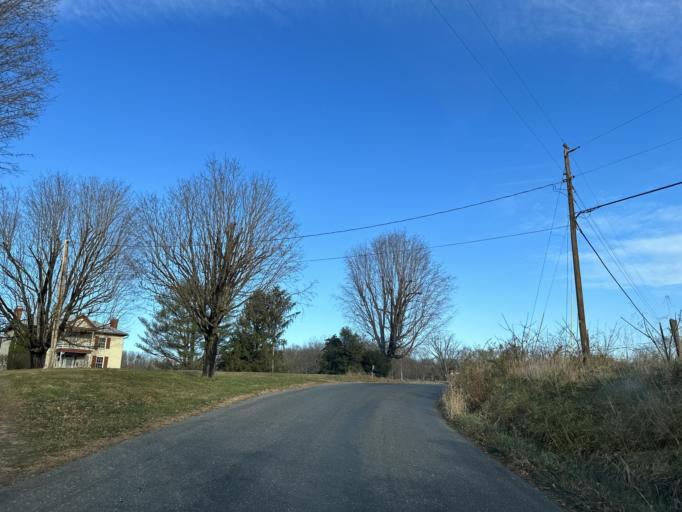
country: US
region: Virginia
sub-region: City of Staunton
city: Staunton
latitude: 38.2308
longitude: -79.2077
